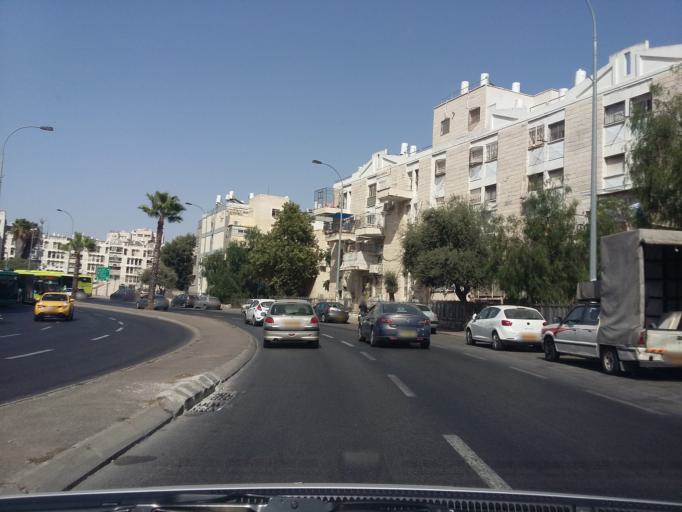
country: IL
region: Jerusalem
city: West Jerusalem
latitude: 31.7963
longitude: 35.2215
